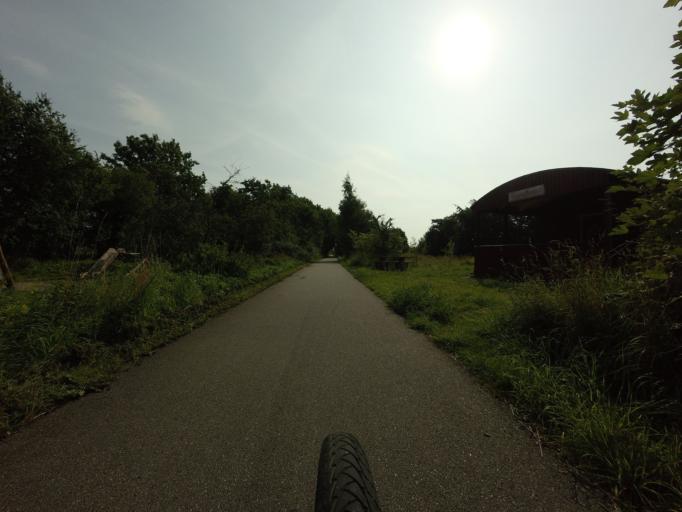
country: DK
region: Zealand
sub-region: Naestved Kommune
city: Fuglebjerg
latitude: 55.2645
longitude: 11.5223
